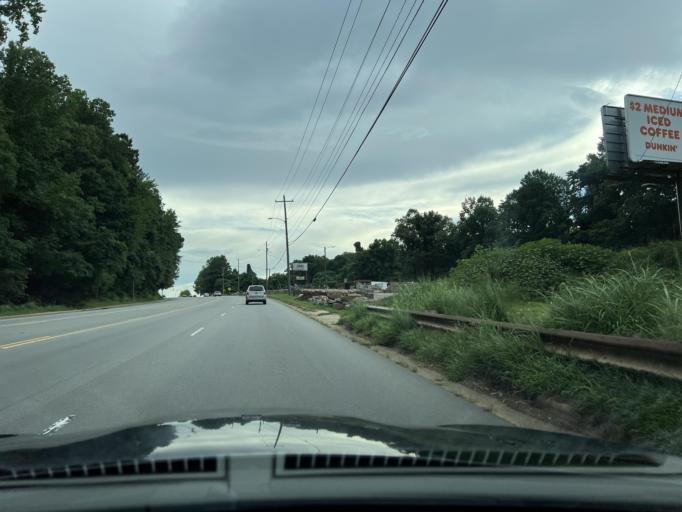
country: US
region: North Carolina
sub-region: Buncombe County
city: Bent Creek
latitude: 35.5692
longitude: -82.6222
